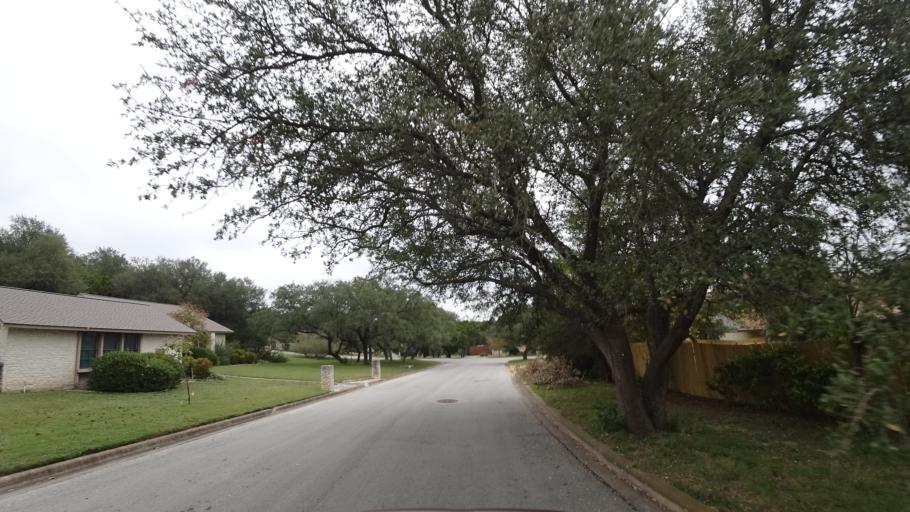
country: US
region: Texas
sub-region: Williamson County
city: Anderson Mill
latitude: 30.4414
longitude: -97.8145
